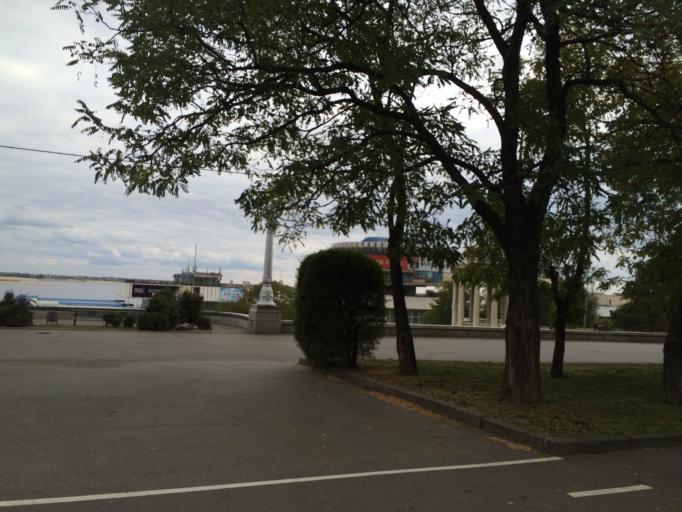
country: RU
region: Volgograd
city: Volgograd
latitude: 48.7030
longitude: 44.5187
